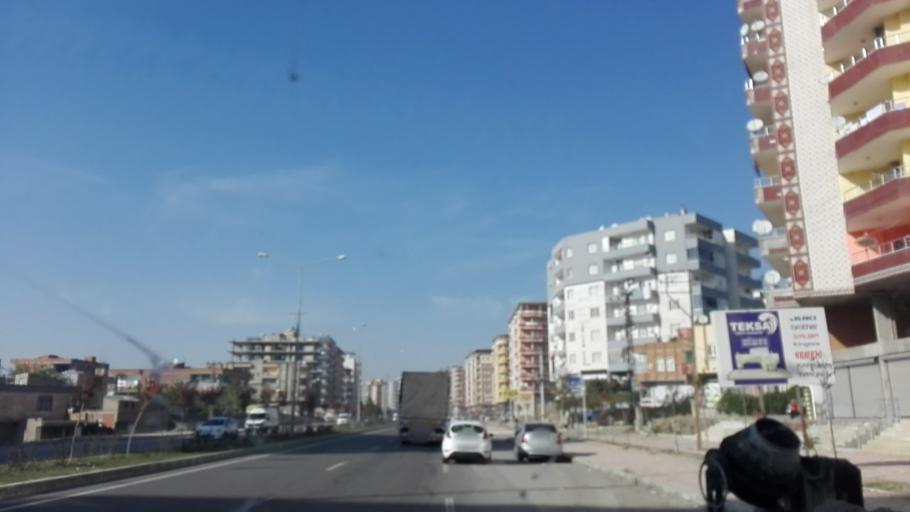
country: TR
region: Batman
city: Aydinkonak
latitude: 37.8963
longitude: 41.1483
